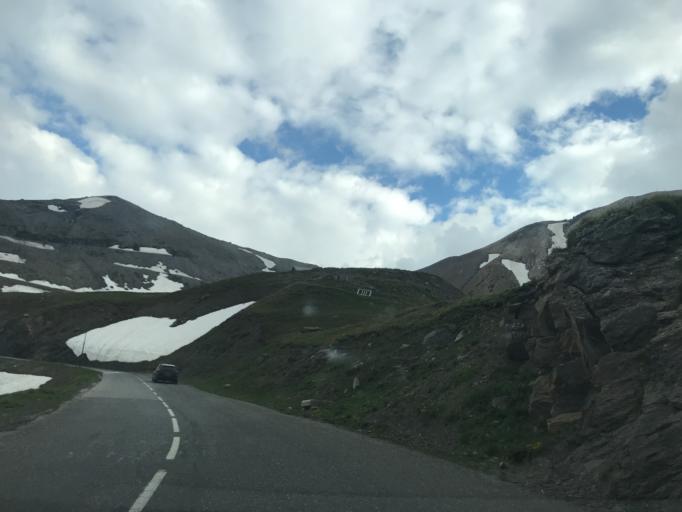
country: FR
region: Rhone-Alpes
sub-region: Departement de la Savoie
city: Valloire
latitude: 45.0683
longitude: 6.4086
